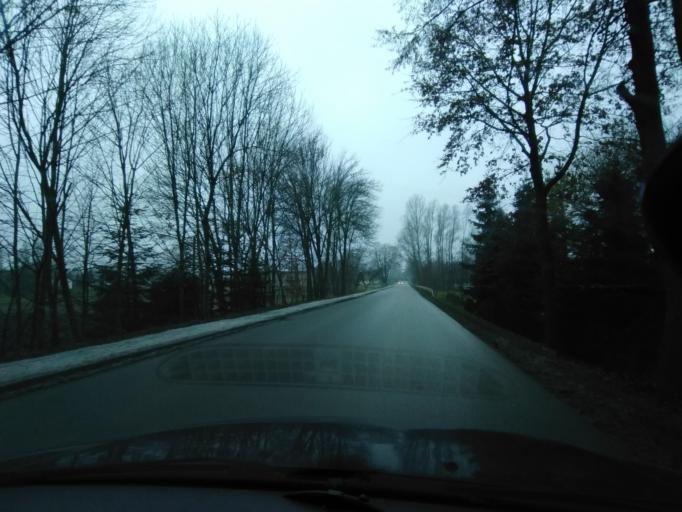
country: PL
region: Subcarpathian Voivodeship
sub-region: Powiat lancucki
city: Markowa
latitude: 50.0268
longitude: 22.3430
